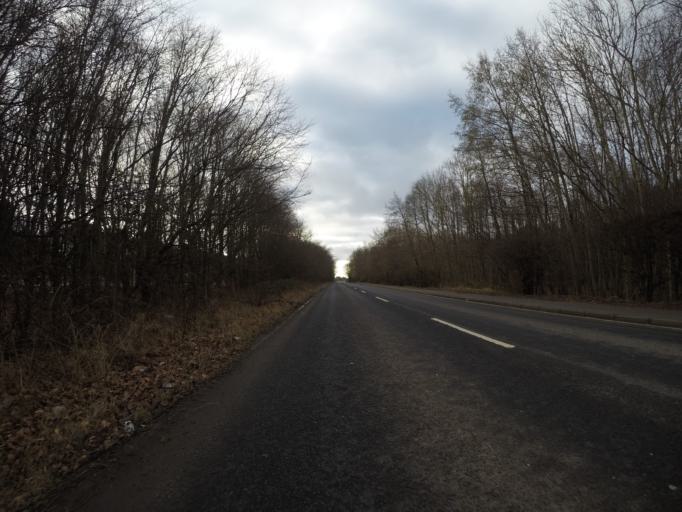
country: GB
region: Scotland
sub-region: North Ayrshire
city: Dreghorn
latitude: 55.5798
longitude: -4.6436
